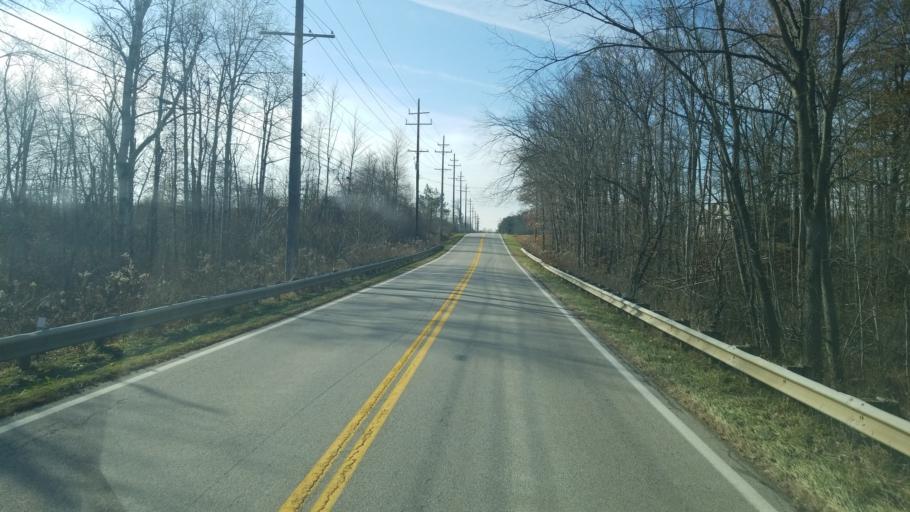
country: US
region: Ohio
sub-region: Ashtabula County
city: Jefferson
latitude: 41.7300
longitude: -80.8085
